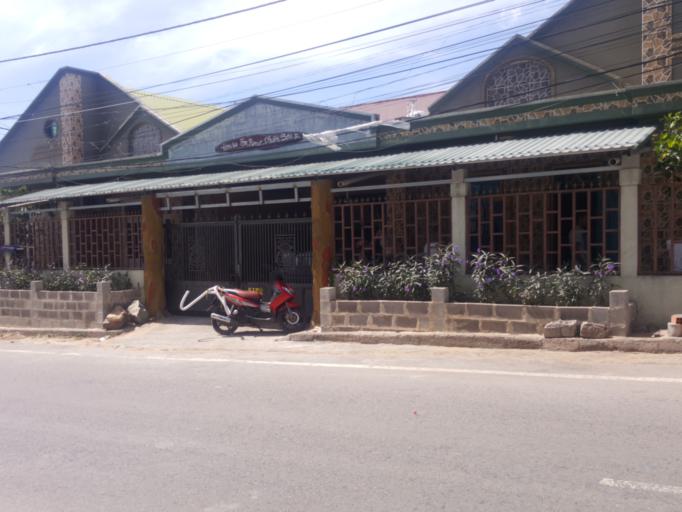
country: VN
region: Binh Thuan
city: Phan Thiet
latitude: 10.9552
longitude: 108.2153
